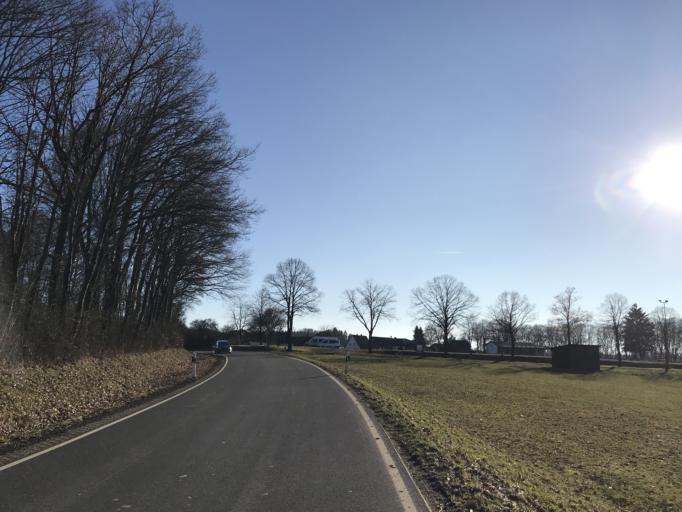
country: DE
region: Hesse
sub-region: Regierungsbezirk Giessen
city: Rabenau
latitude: 50.6613
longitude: 8.8512
